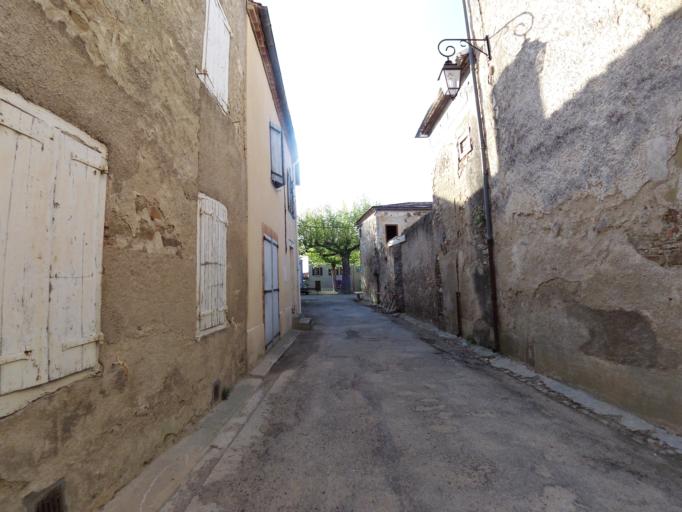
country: FR
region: Midi-Pyrenees
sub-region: Departement du Tarn
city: Soreze
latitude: 43.4520
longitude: 2.0657
